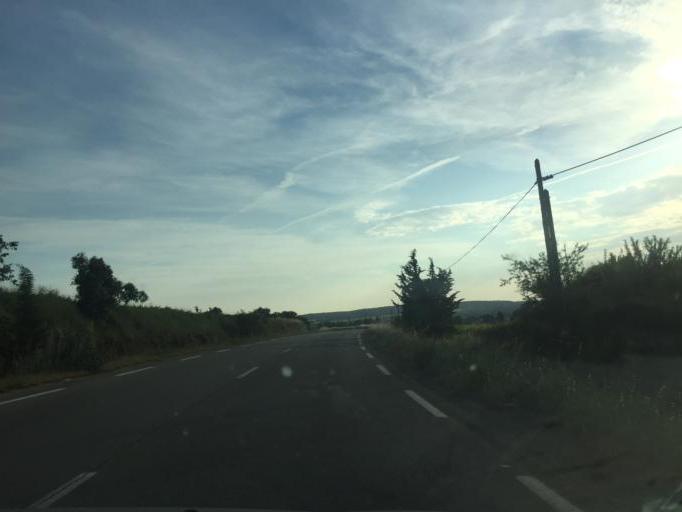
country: FR
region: Languedoc-Roussillon
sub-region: Departement du Gard
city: Roquemaure
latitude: 44.0281
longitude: 4.7557
